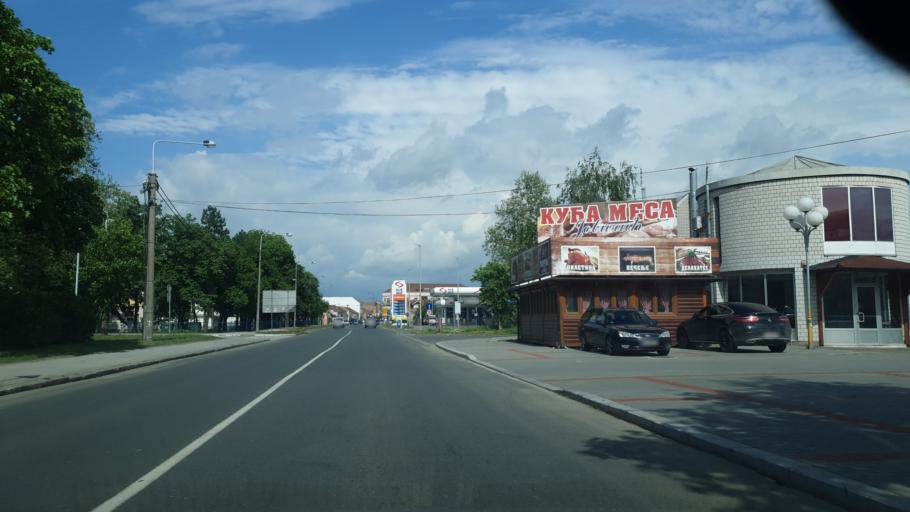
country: RS
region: Central Serbia
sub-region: Belgrade
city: Obrenovac
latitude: 44.6499
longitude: 20.1918
